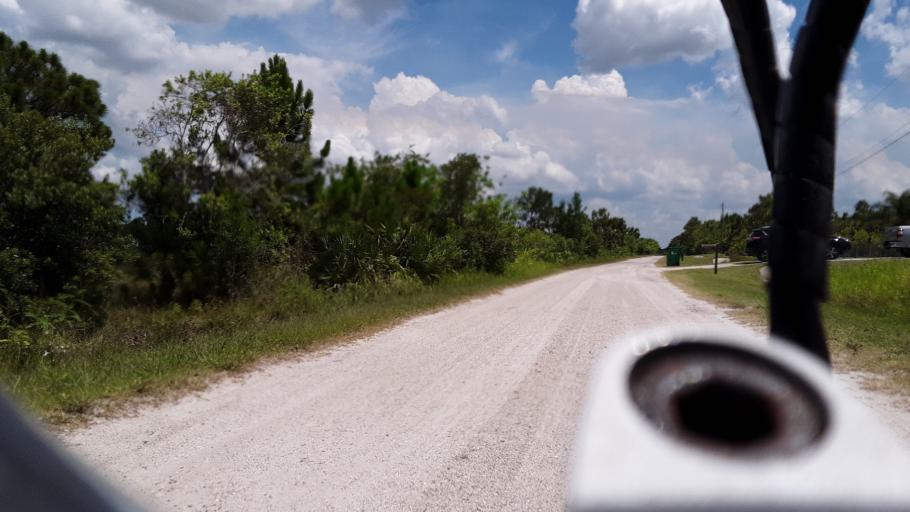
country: US
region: Florida
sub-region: Brevard County
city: Malabar
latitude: 27.9880
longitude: -80.5732
